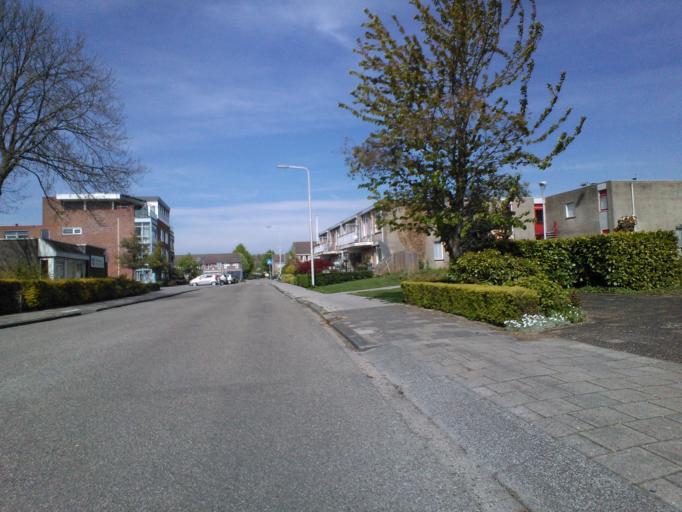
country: NL
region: South Holland
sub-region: Bodegraven-Reeuwijk
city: Reeuwijk
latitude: 52.0446
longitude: 4.7301
